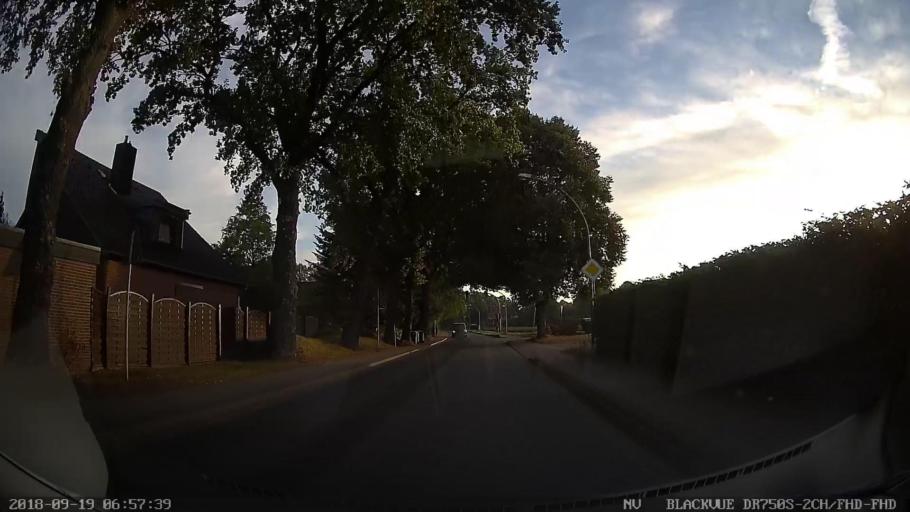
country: DE
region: Schleswig-Holstein
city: Ellerbek
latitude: 53.6352
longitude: 9.8769
